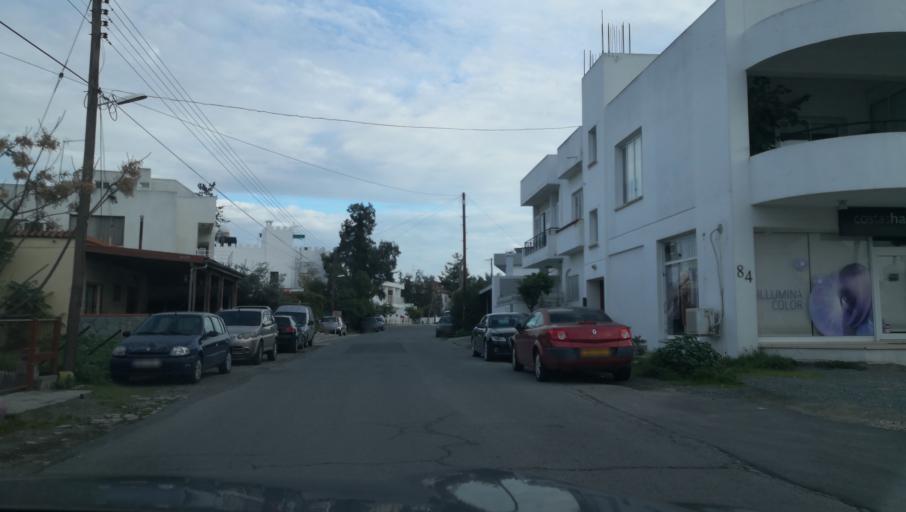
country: CY
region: Lefkosia
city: Nicosia
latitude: 35.1359
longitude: 33.3498
